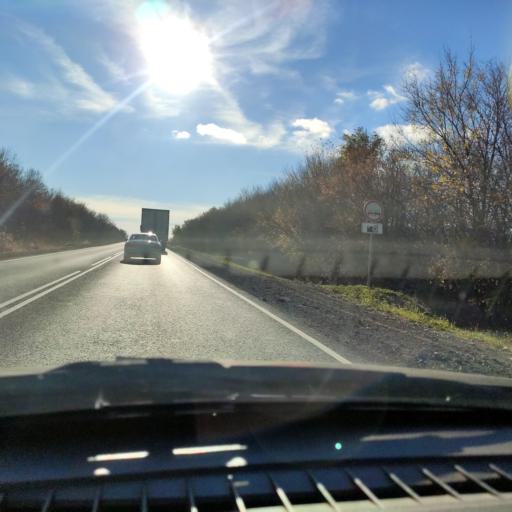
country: RU
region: Samara
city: Zhigulevsk
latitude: 53.3130
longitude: 49.3592
